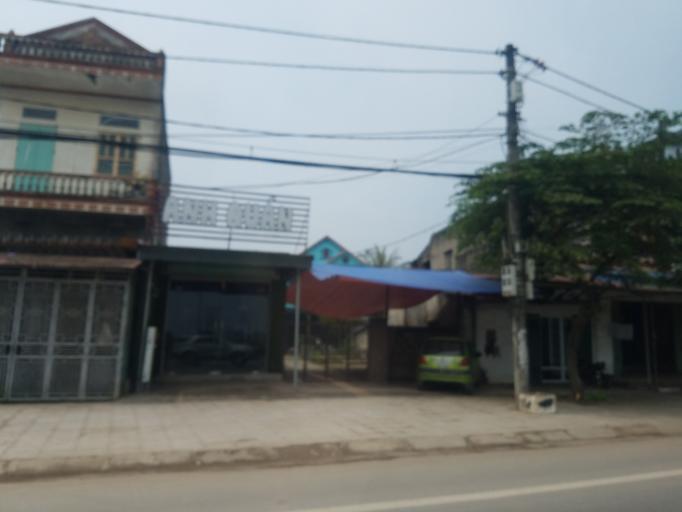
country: VN
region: Thai Nguyen
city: Chua Hang
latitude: 21.6092
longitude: 105.8397
